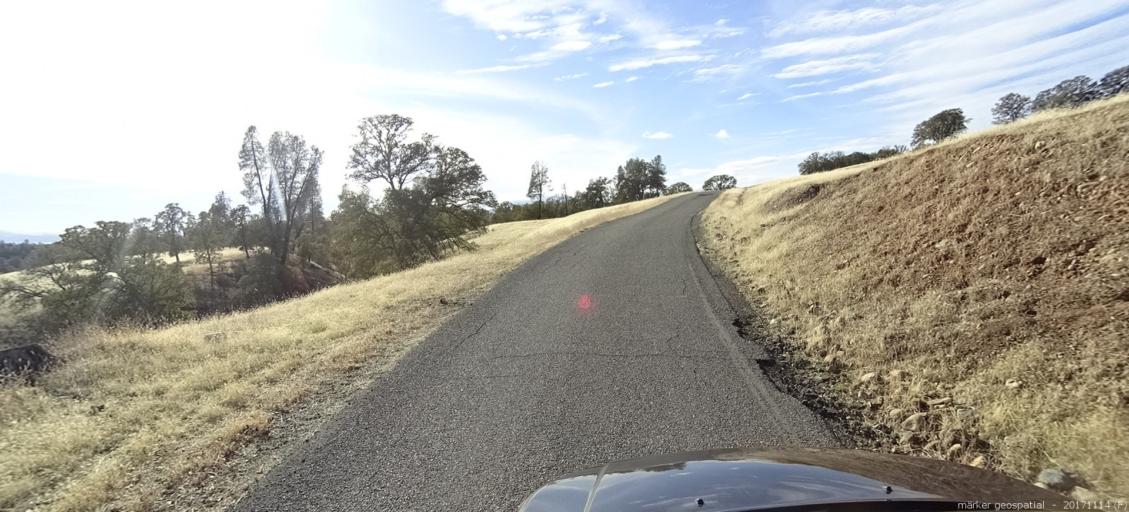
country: US
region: California
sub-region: Shasta County
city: Shasta
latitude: 40.3714
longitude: -122.5656
